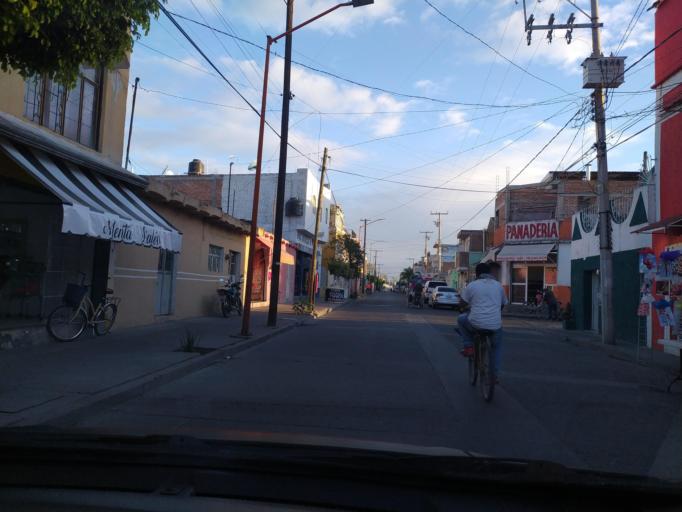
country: MX
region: Guanajuato
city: San Francisco del Rincon
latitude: 21.0125
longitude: -101.8525
